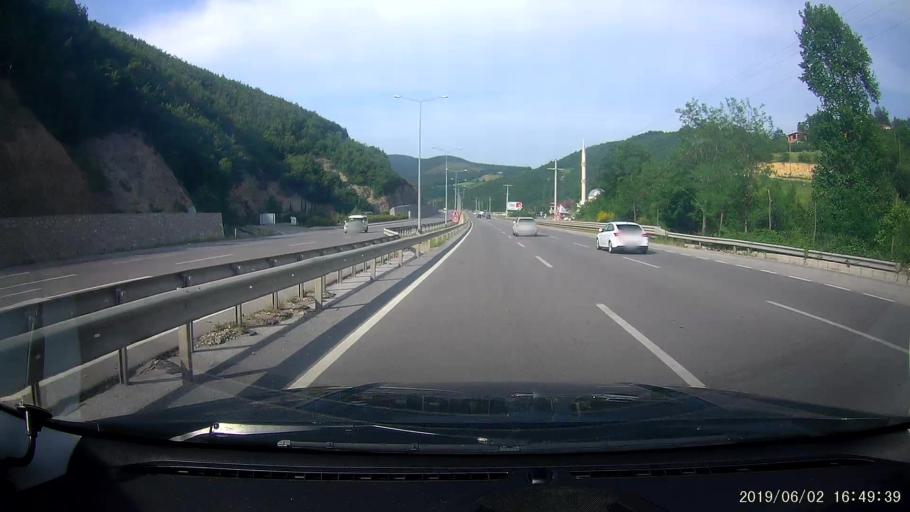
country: TR
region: Samsun
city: Samsun
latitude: 41.2404
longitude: 36.1663
